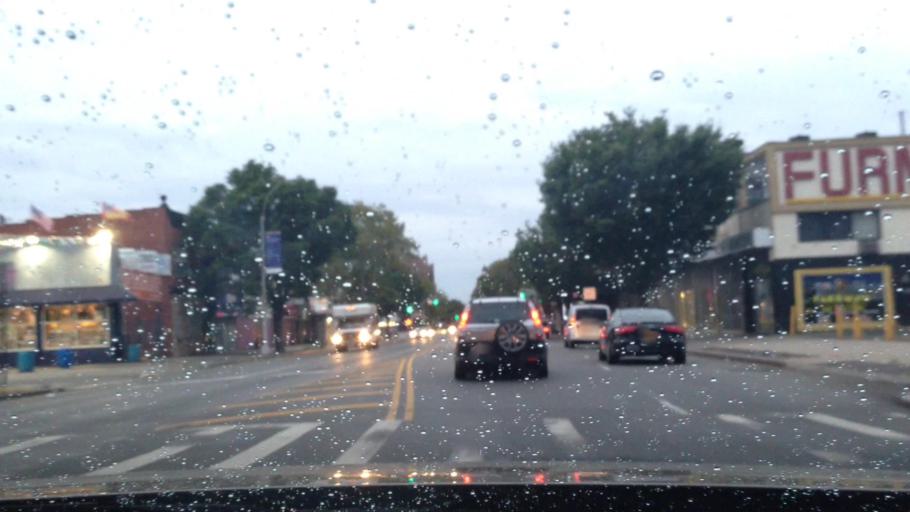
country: US
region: New York
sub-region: Kings County
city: East New York
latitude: 40.6772
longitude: -73.8973
